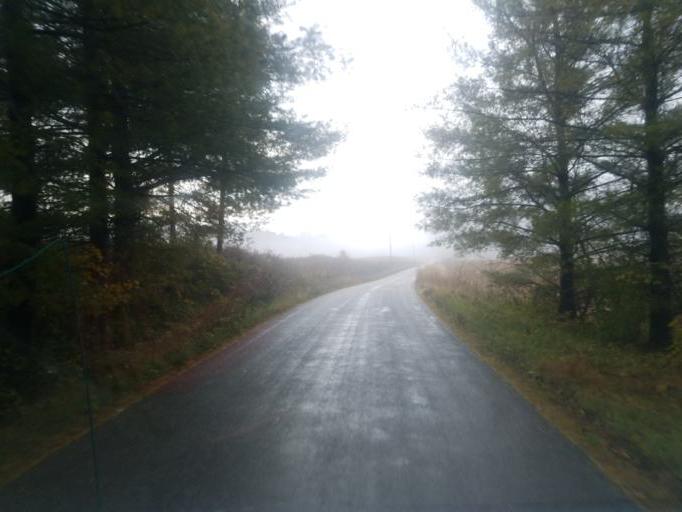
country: US
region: Ohio
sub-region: Athens County
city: Glouster
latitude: 39.4678
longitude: -81.9383
